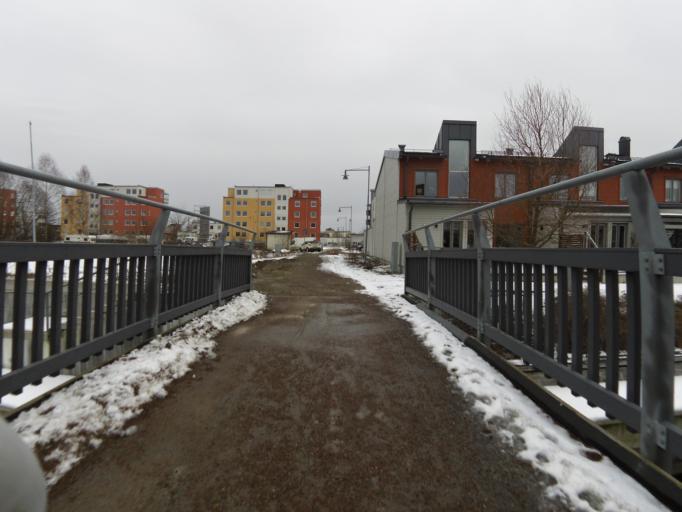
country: SE
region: Gaevleborg
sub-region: Gavle Kommun
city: Gavle
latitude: 60.6802
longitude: 17.1663
